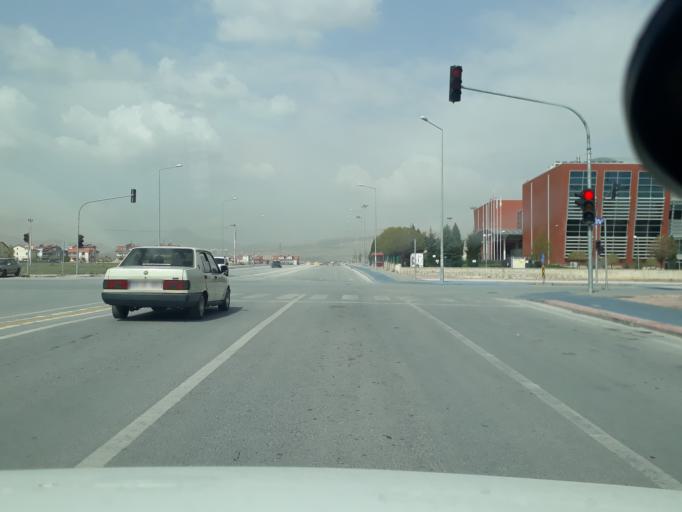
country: TR
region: Konya
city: Selcuklu
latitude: 37.9425
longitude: 32.4902
